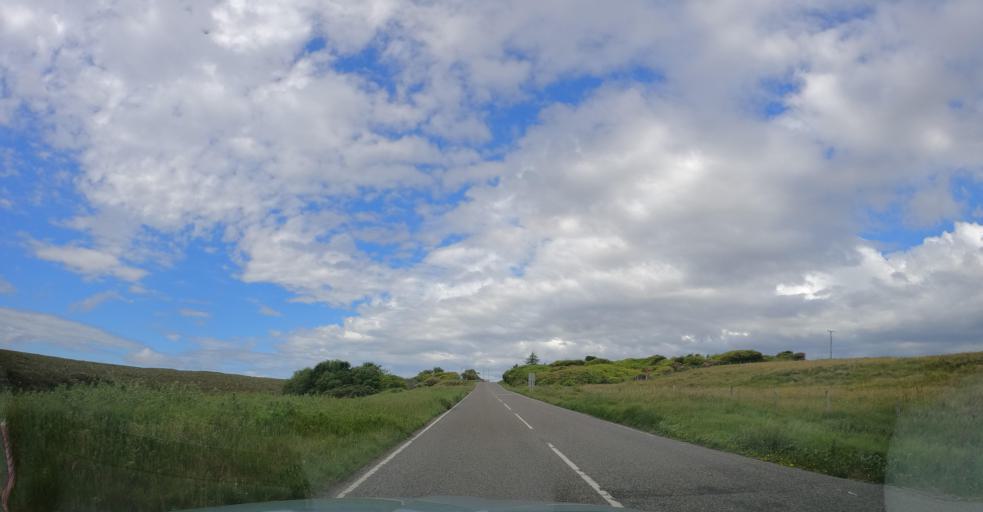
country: GB
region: Scotland
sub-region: Eilean Siar
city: Isle of Lewis
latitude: 58.2483
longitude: -6.4047
